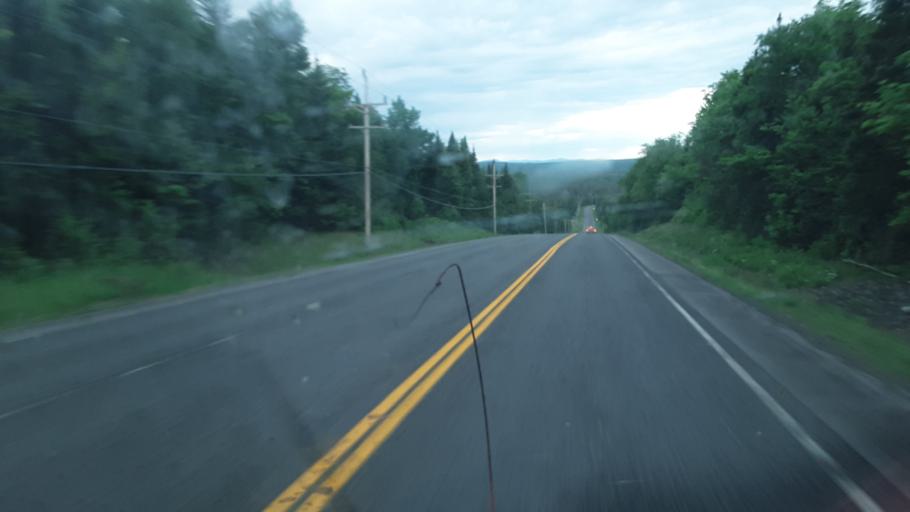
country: US
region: Maine
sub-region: Aroostook County
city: Presque Isle
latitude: 46.6631
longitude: -68.2315
